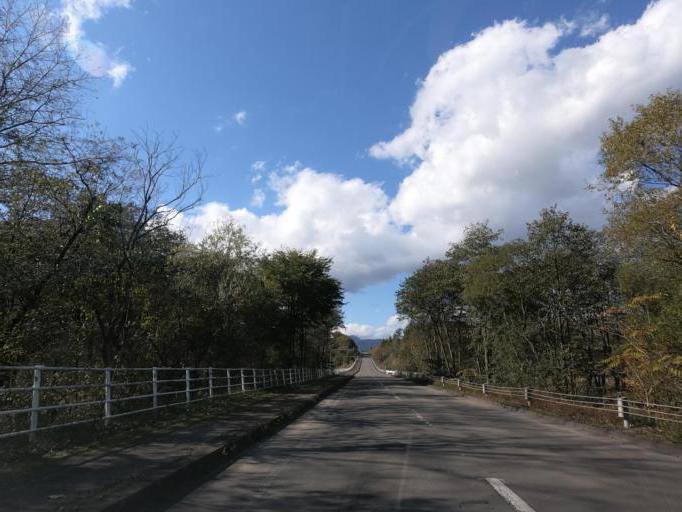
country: JP
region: Hokkaido
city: Otofuke
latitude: 43.2384
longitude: 143.2705
